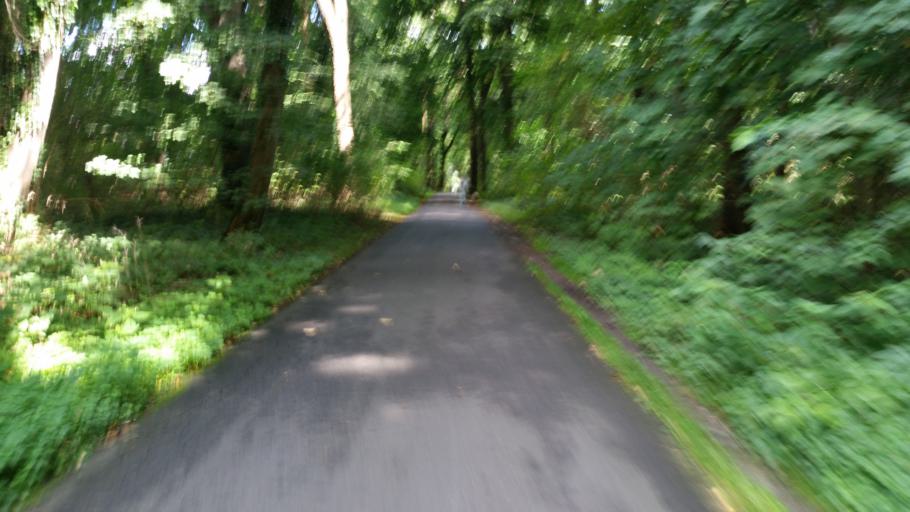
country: DE
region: Lower Saxony
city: Hannover
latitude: 52.3923
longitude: 9.7624
